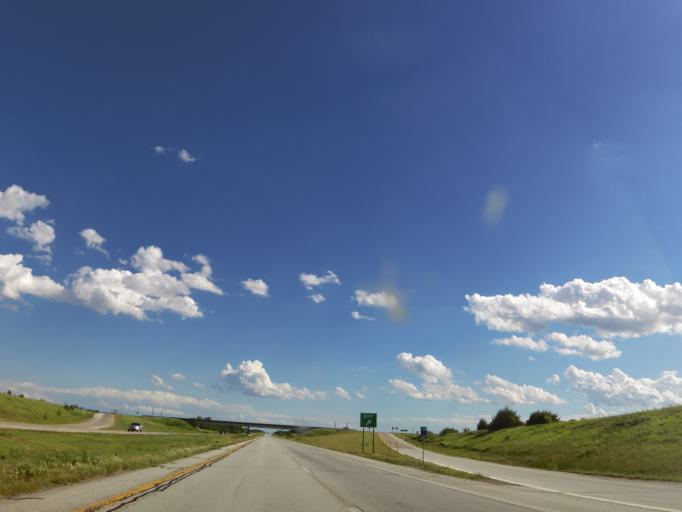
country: US
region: Missouri
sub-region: Lewis County
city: Canton
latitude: 40.0512
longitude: -91.5252
